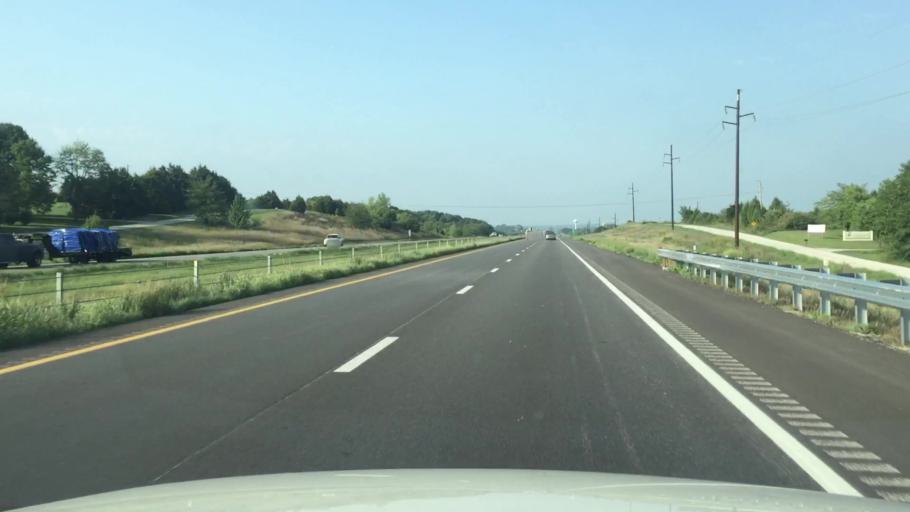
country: US
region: Missouri
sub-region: Clay County
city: Kearney
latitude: 39.3345
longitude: -94.3900
